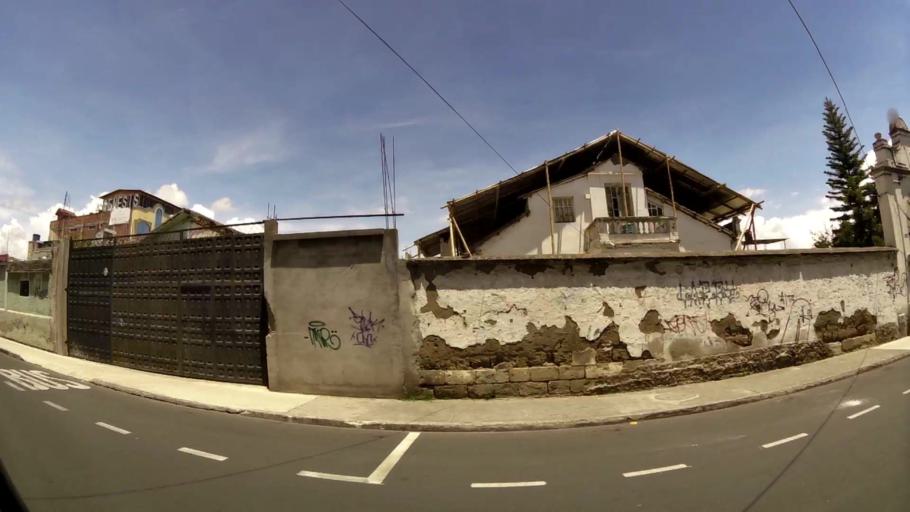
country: EC
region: Chimborazo
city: Riobamba
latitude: -1.6675
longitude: -78.6479
